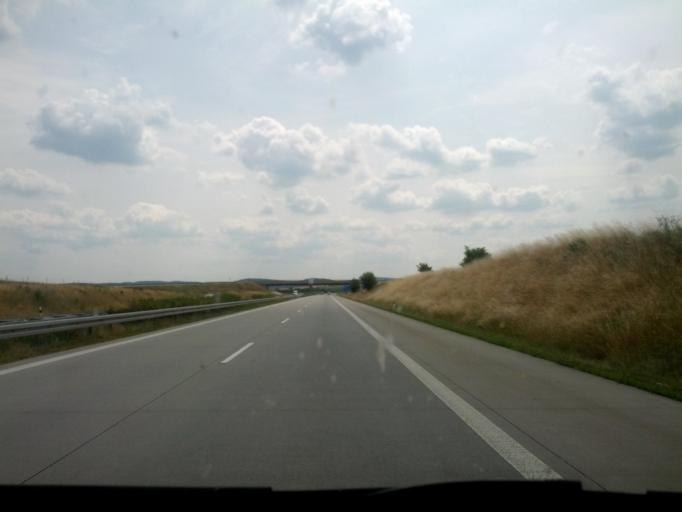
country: DE
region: Saxony
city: Dohma
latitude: 50.9119
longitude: 13.8928
